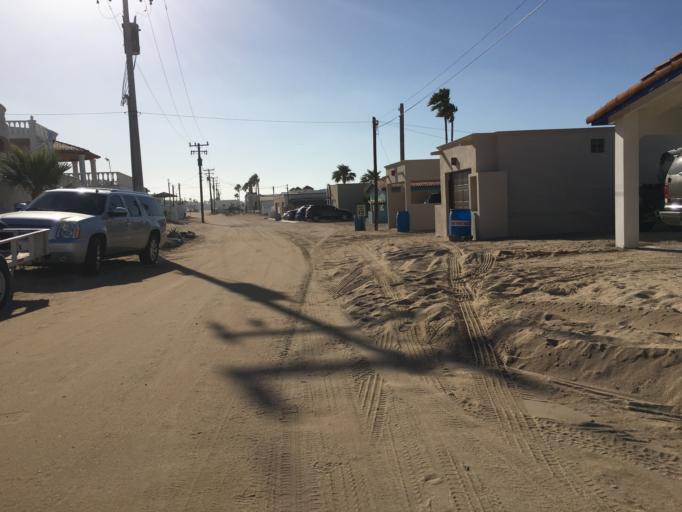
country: MX
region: Sonora
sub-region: Puerto Penasco
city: Puerto Penasco
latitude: 31.2907
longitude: -113.5000
